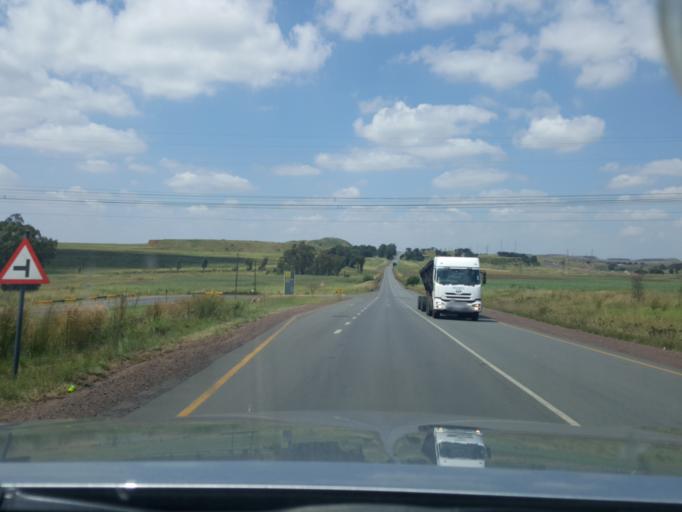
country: ZA
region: Mpumalanga
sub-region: Nkangala District Municipality
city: Witbank
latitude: -26.0141
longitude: 29.3628
